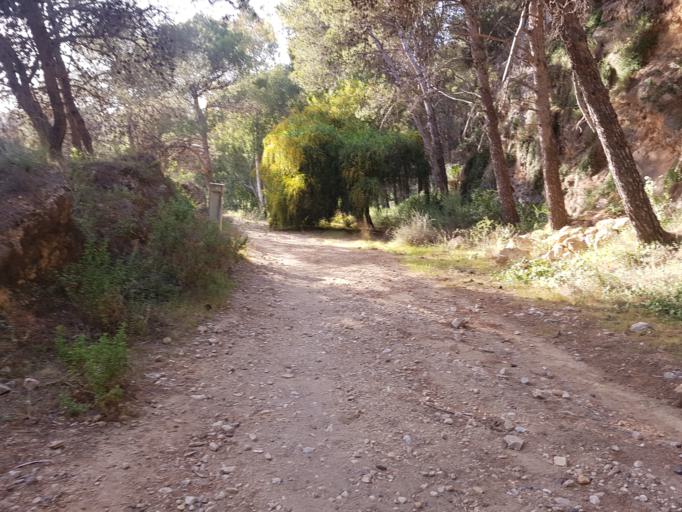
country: ES
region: Andalusia
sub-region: Provincia de Malaga
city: Marbella
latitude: 36.5296
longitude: -4.8821
